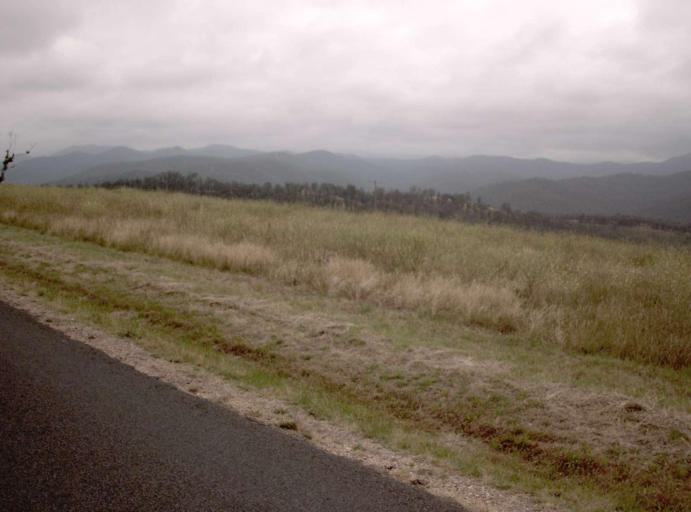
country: AU
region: Victoria
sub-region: Wellington
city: Heyfield
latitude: -37.8363
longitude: 146.6825
